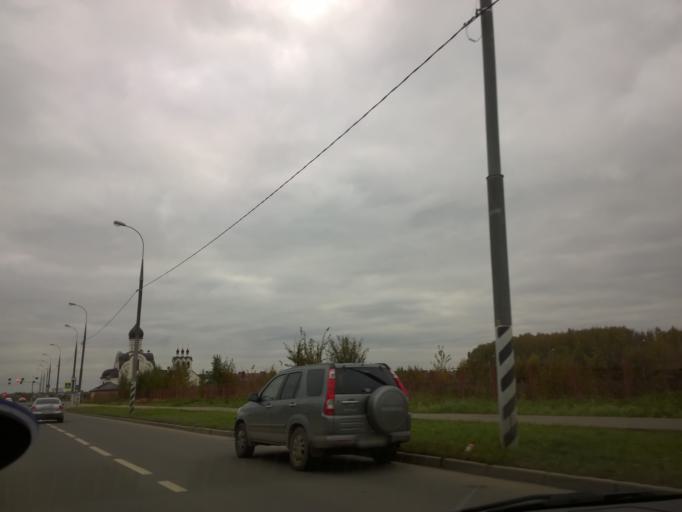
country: RU
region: Moskovskaya
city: Kommunarka
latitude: 55.5333
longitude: 37.4992
